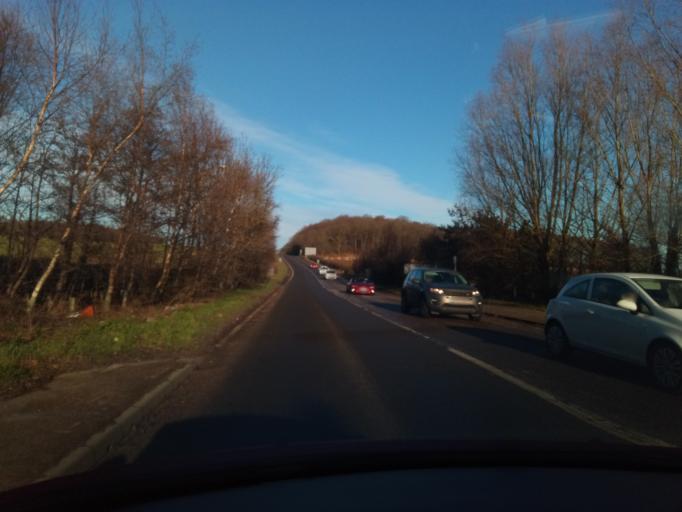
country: GB
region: England
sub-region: Nottinghamshire
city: Boughton
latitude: 53.2436
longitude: -1.0254
